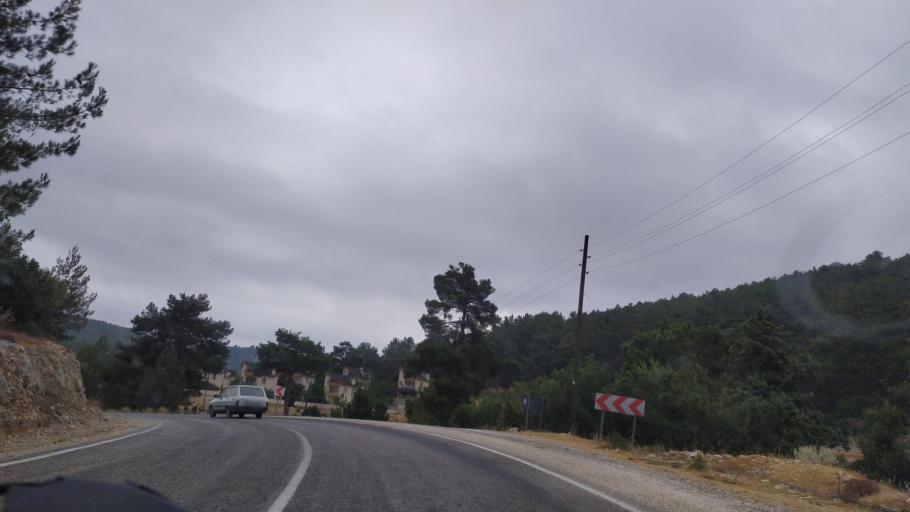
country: TR
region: Mersin
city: Silifke
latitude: 36.5402
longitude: 33.9402
